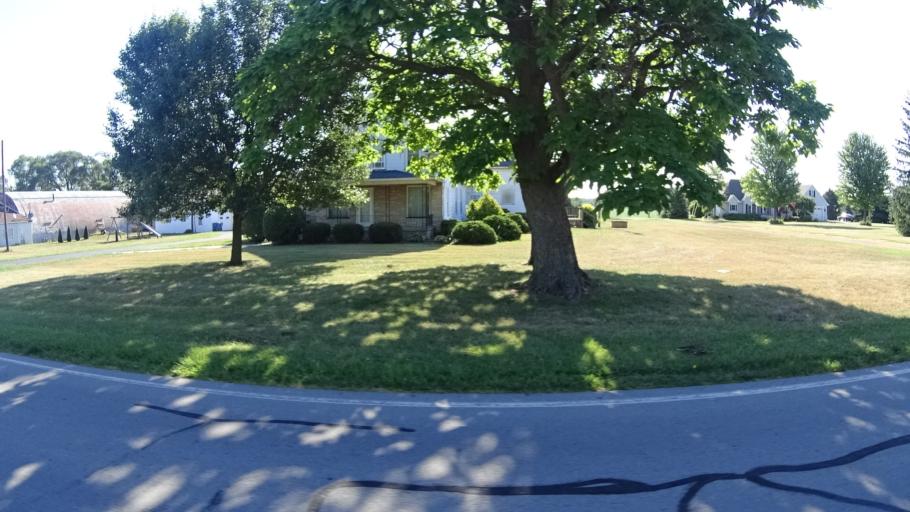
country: US
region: Ohio
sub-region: Erie County
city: Sandusky
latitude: 41.4049
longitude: -82.7714
